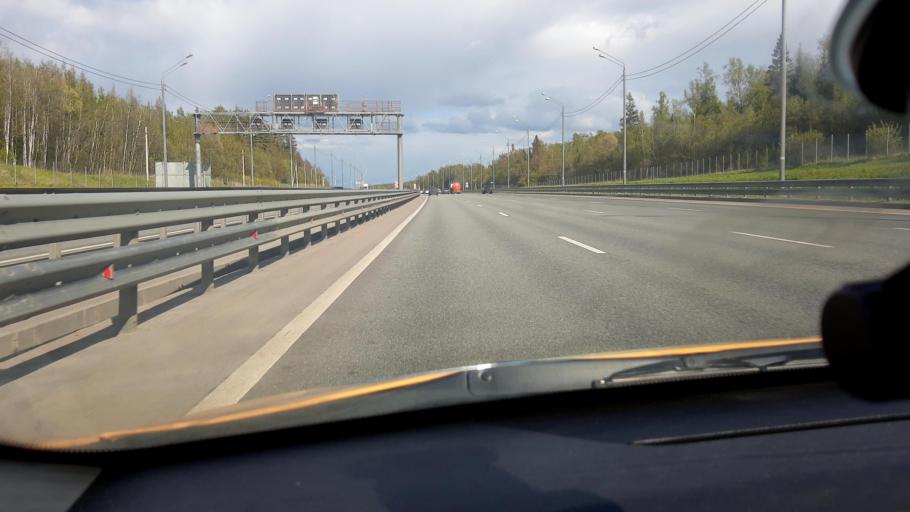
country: RU
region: Moskovskaya
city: Yershovo
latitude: 55.8198
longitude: 36.9438
